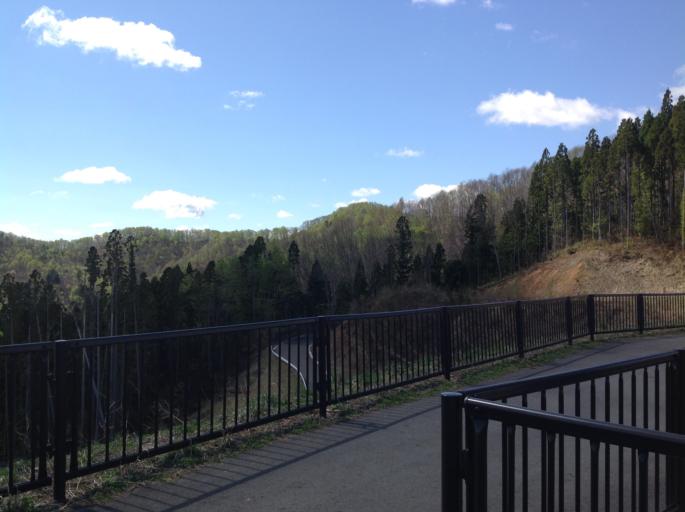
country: JP
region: Iwate
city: Mizusawa
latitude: 39.1159
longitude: 140.9198
